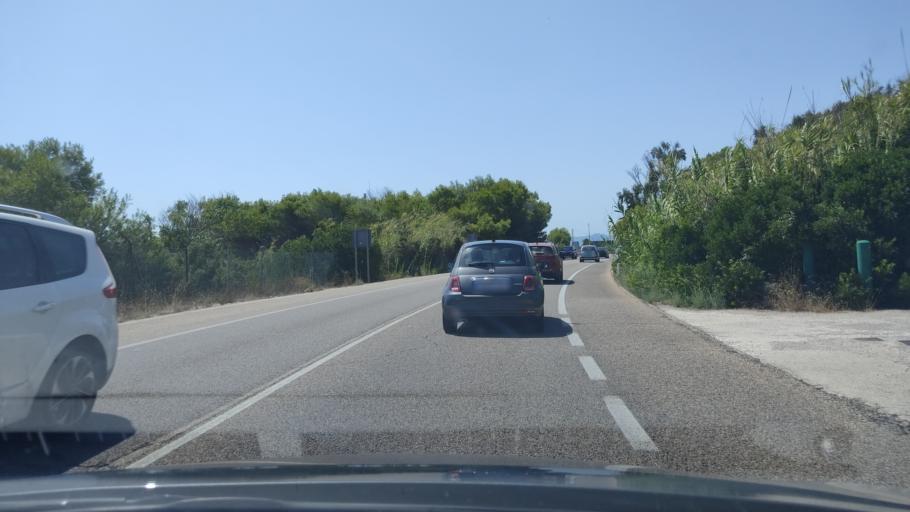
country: ES
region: Valencia
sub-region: Provincia de Valencia
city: Sollana
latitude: 39.3111
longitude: -0.2992
